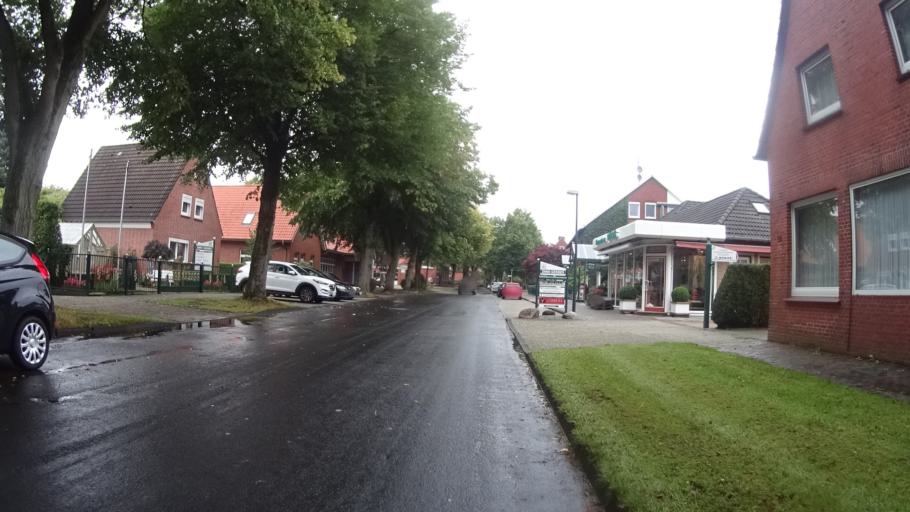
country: DE
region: Lower Saxony
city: Leer
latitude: 53.2346
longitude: 7.4479
